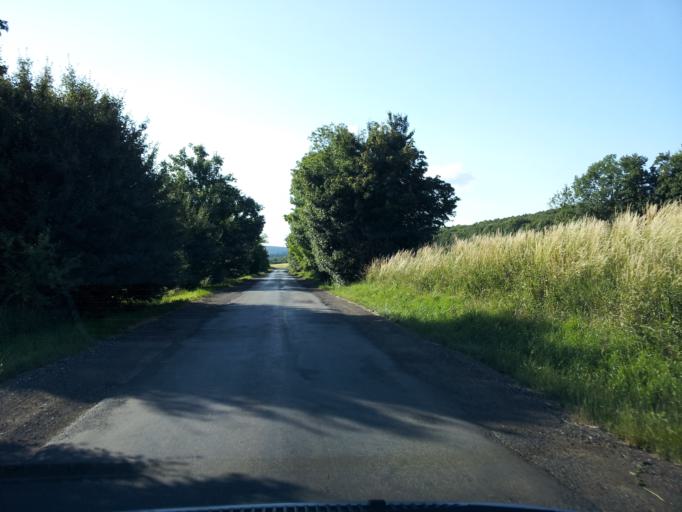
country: HU
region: Veszprem
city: Zirc
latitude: 47.2108
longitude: 17.8449
